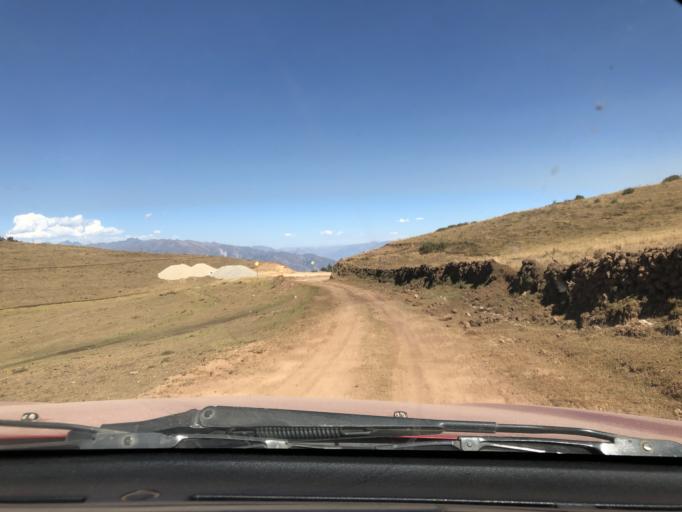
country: PE
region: Ayacucho
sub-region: Provincia de La Mar
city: Pampas
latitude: -13.1882
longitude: -73.8433
